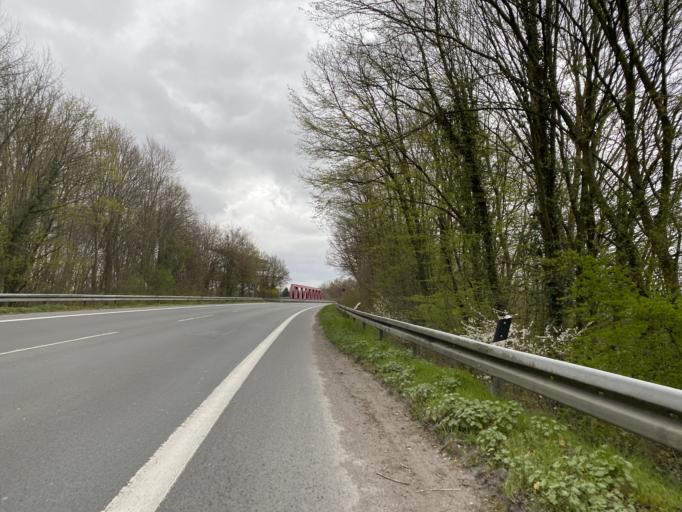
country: DE
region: North Rhine-Westphalia
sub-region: Regierungsbezirk Arnsberg
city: Welver
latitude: 51.6830
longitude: 7.9440
